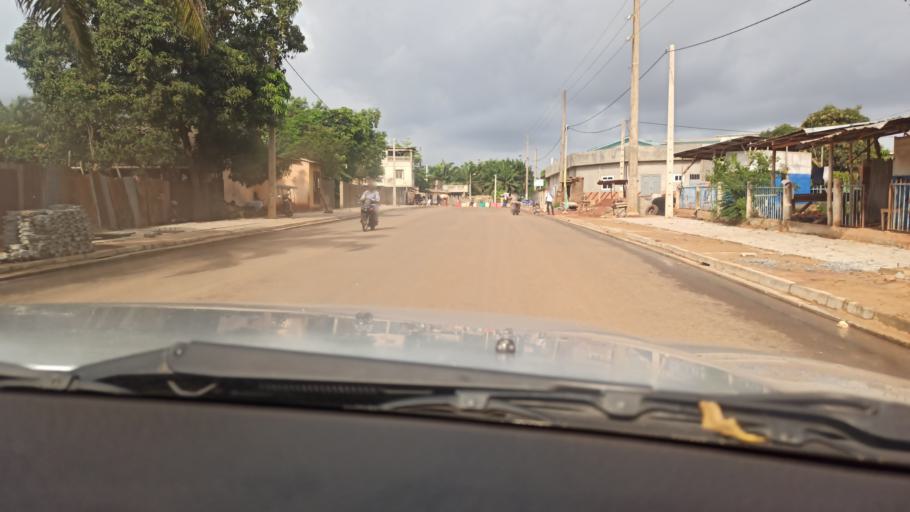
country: BJ
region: Queme
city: Porto-Novo
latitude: 6.5179
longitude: 2.6000
